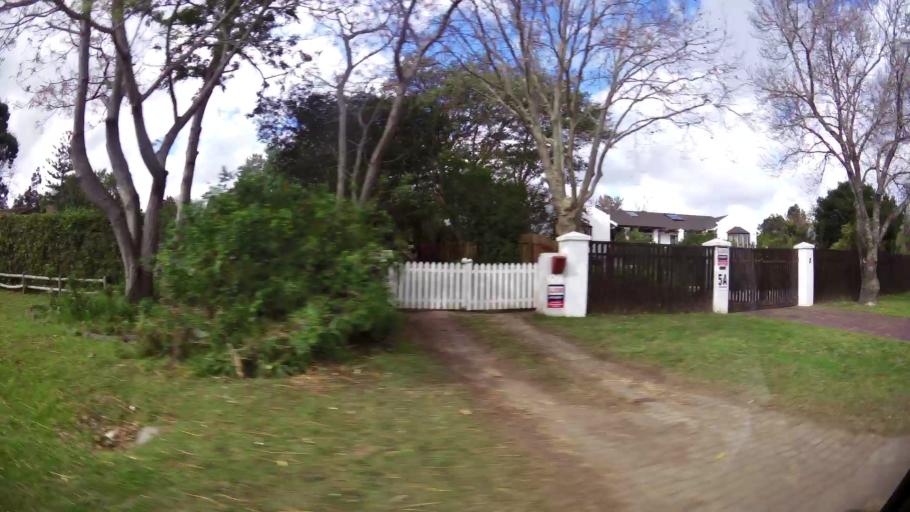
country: ZA
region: Western Cape
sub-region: Eden District Municipality
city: Knysna
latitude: -34.0614
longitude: 23.0797
